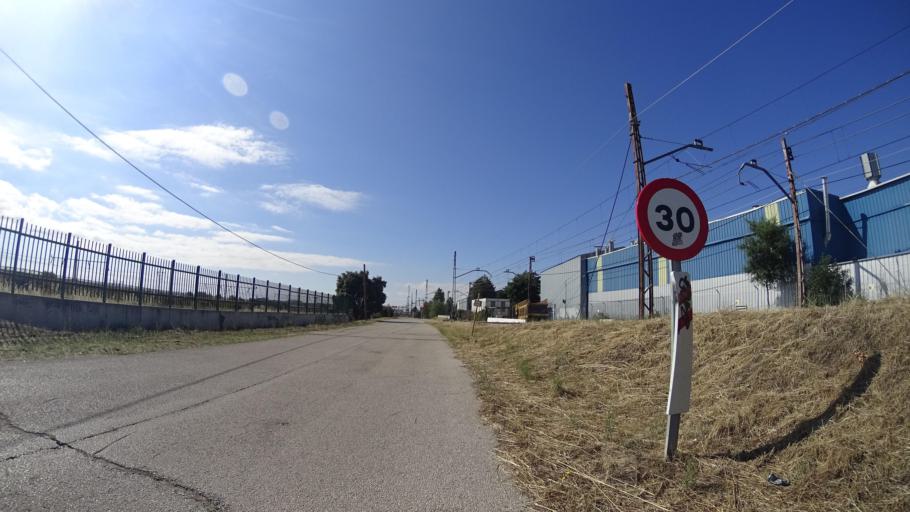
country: ES
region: Madrid
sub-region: Provincia de Madrid
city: Las Matas
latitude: 40.5406
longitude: -3.8903
